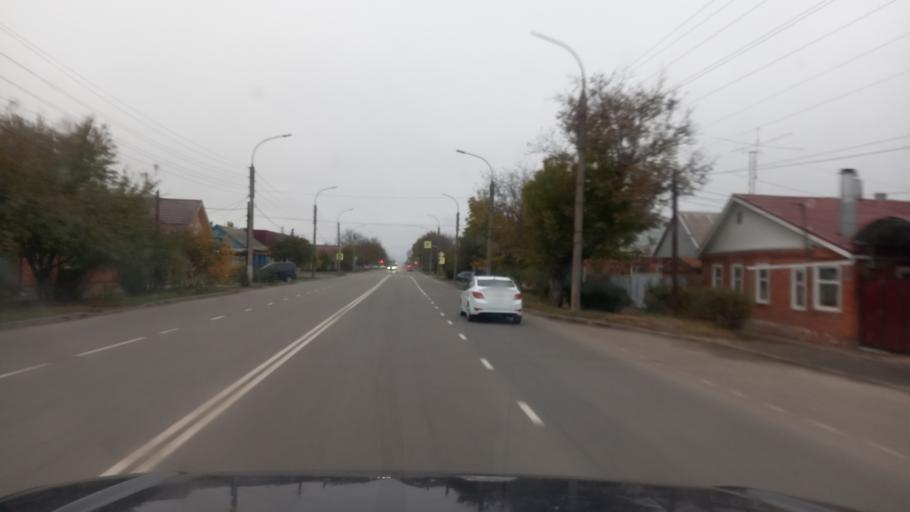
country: RU
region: Adygeya
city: Maykop
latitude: 44.6183
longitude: 40.0990
